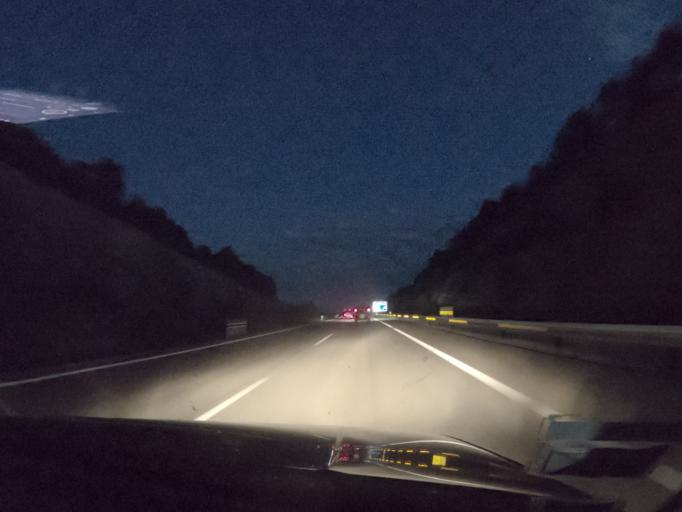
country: ES
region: Castille and Leon
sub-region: Provincia de Leon
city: Brazuelo
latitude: 42.5404
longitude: -6.1573
